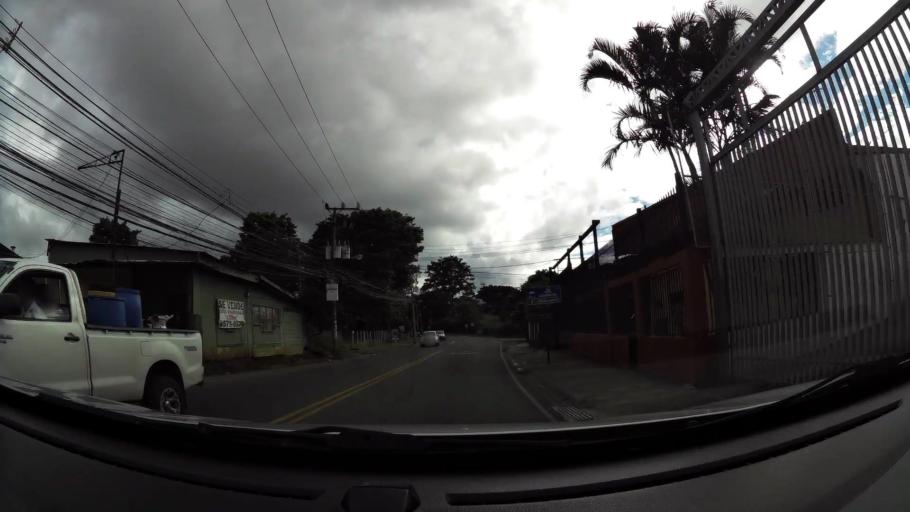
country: CR
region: San Jose
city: Curridabat
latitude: 9.9117
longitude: -84.0441
